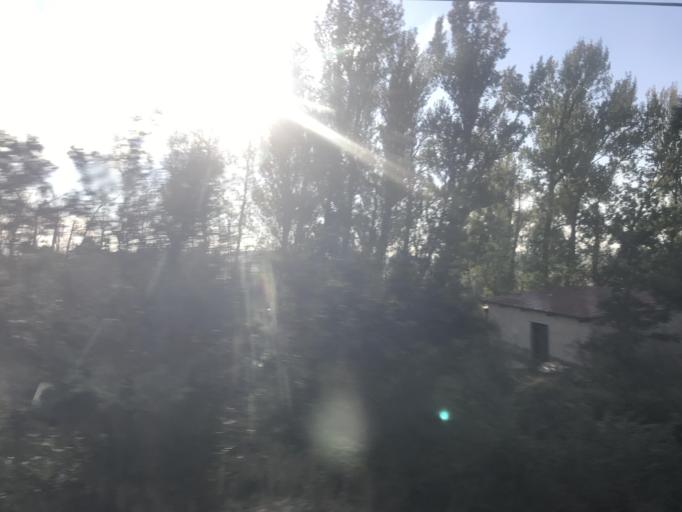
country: ES
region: Castille and Leon
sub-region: Provincia de Burgos
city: Villazopeque
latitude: 42.2081
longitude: -4.0093
